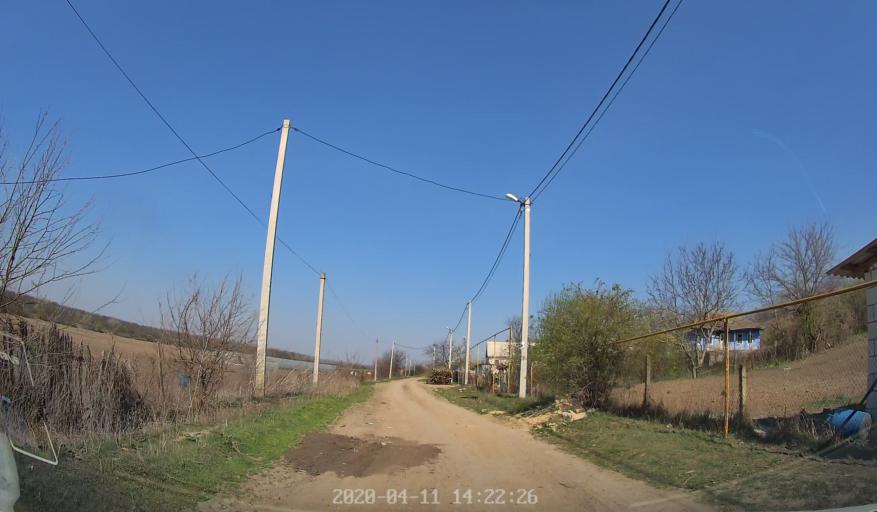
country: MD
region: Chisinau
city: Vadul lui Voda
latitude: 47.0887
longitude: 29.1368
